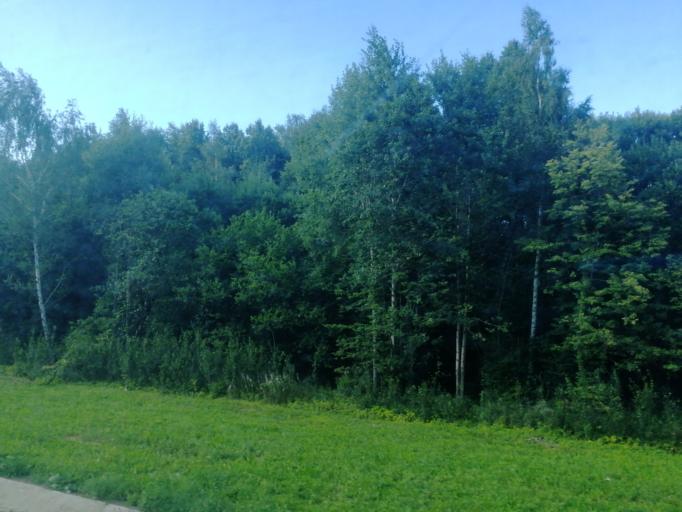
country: RU
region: Tula
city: Leninskiy
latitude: 54.2347
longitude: 37.3550
